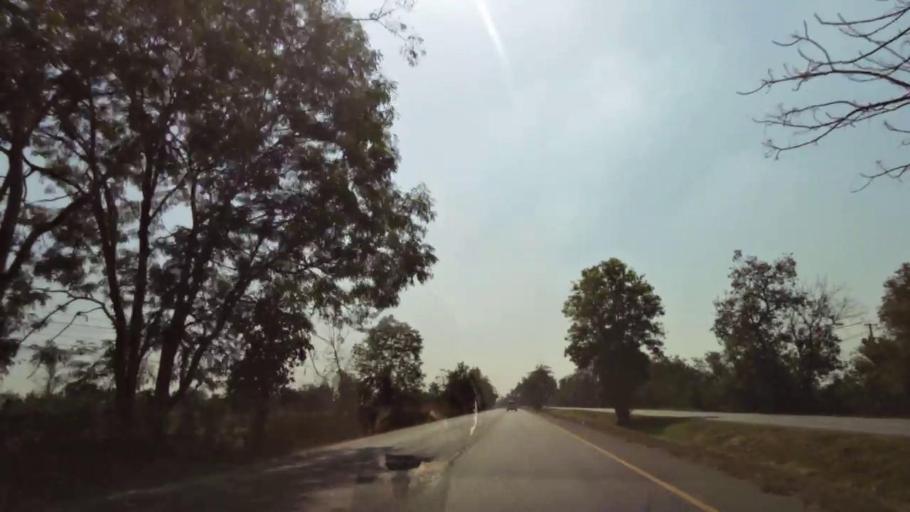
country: TH
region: Phichit
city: Wachira Barami
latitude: 16.3655
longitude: 100.1312
